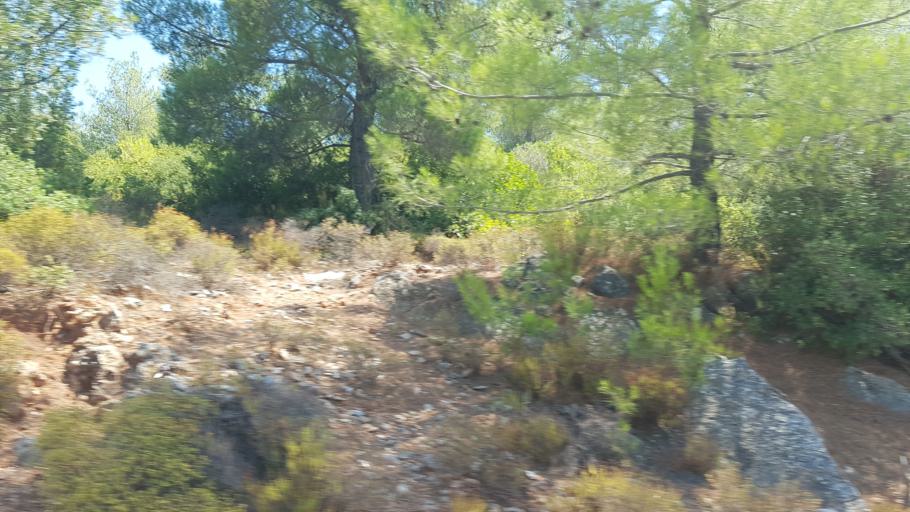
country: TR
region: Mugla
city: Karaova
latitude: 37.0194
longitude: 27.7320
